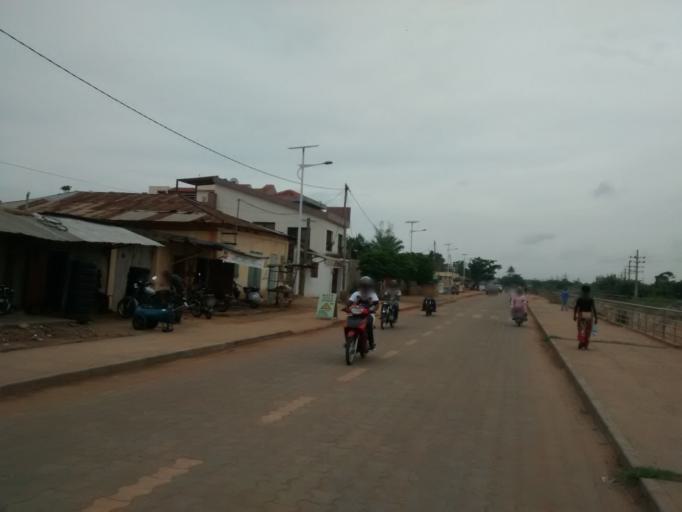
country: TG
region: Maritime
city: Lome
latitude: 6.1508
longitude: 1.2120
